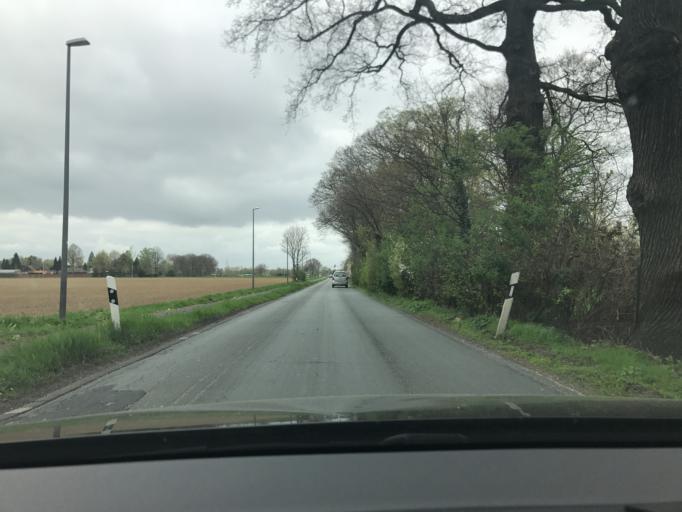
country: DE
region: North Rhine-Westphalia
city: Tonisvorst
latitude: 51.3039
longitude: 6.5273
